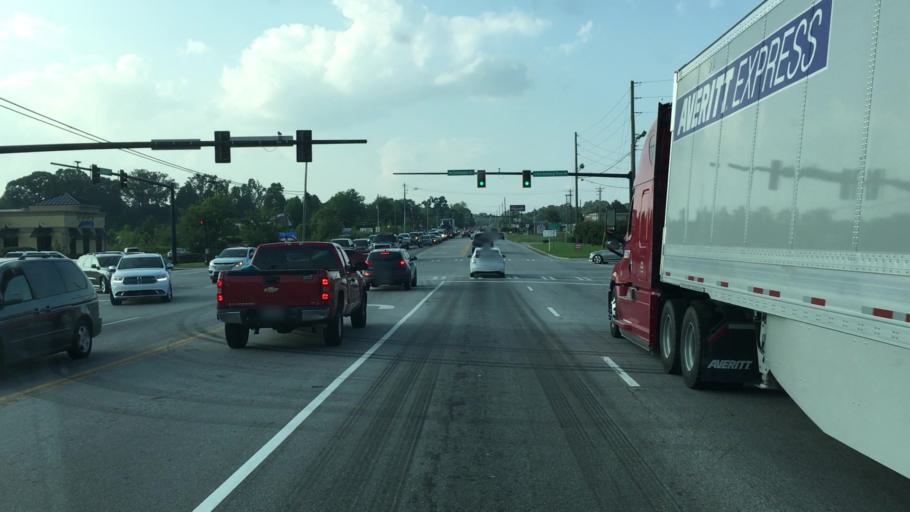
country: US
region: Georgia
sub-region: Jackson County
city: Braselton
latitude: 34.1199
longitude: -83.7629
